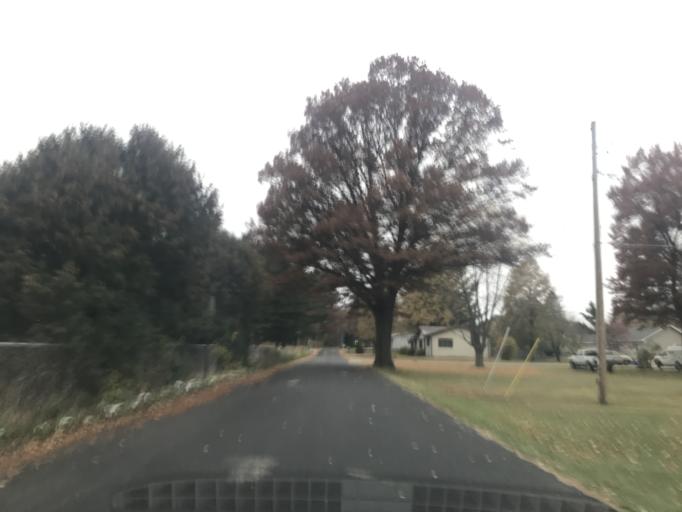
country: US
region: Wisconsin
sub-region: Marinette County
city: Marinette
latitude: 45.0964
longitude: -87.6513
